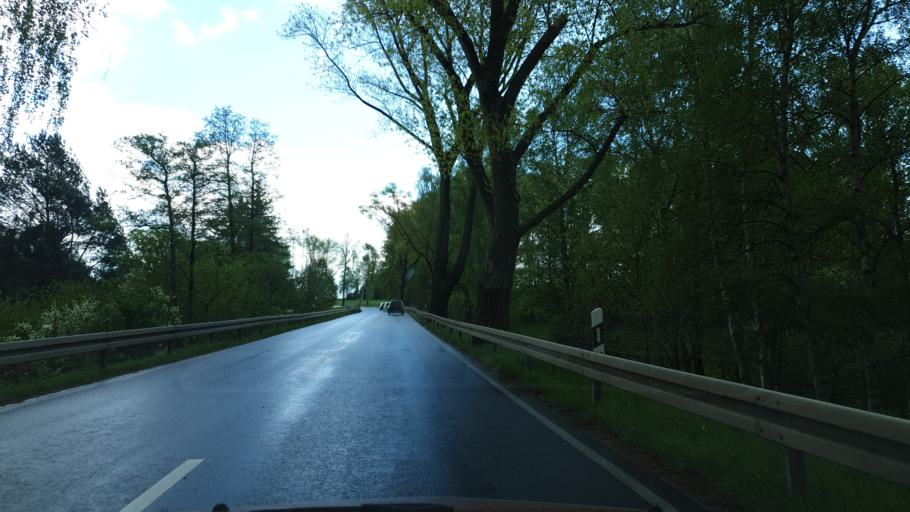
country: DE
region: Saxony
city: Neukirchen
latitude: 50.8078
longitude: 12.8226
